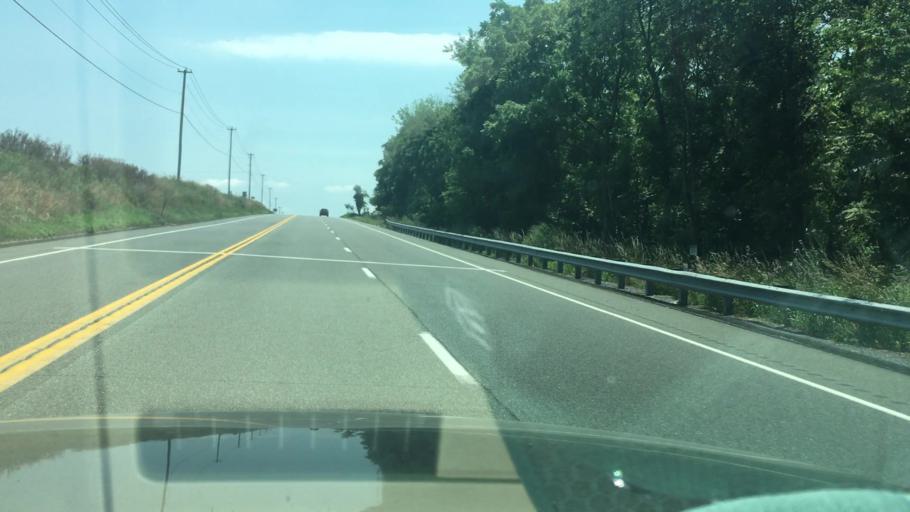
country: US
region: Pennsylvania
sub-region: Lehigh County
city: Schnecksville
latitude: 40.6229
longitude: -75.6653
